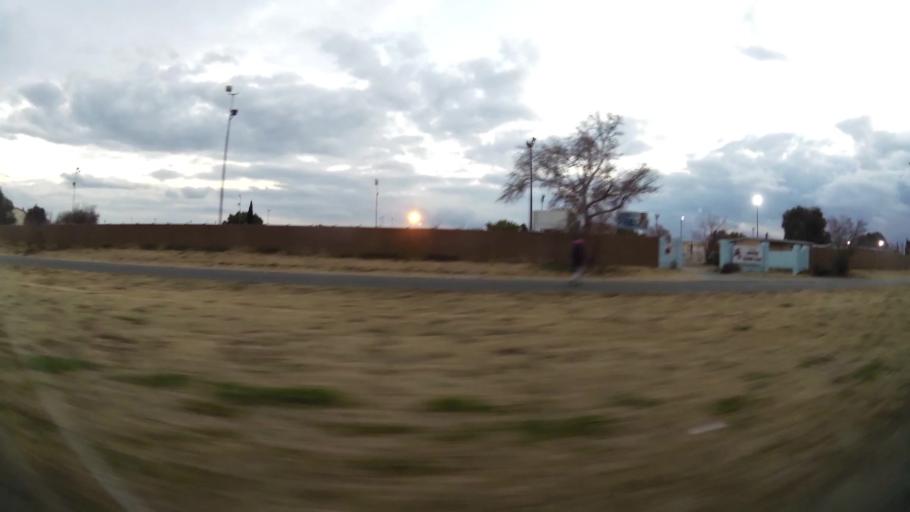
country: ZA
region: Orange Free State
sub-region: Lejweleputswa District Municipality
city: Welkom
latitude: -27.9777
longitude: 26.7545
